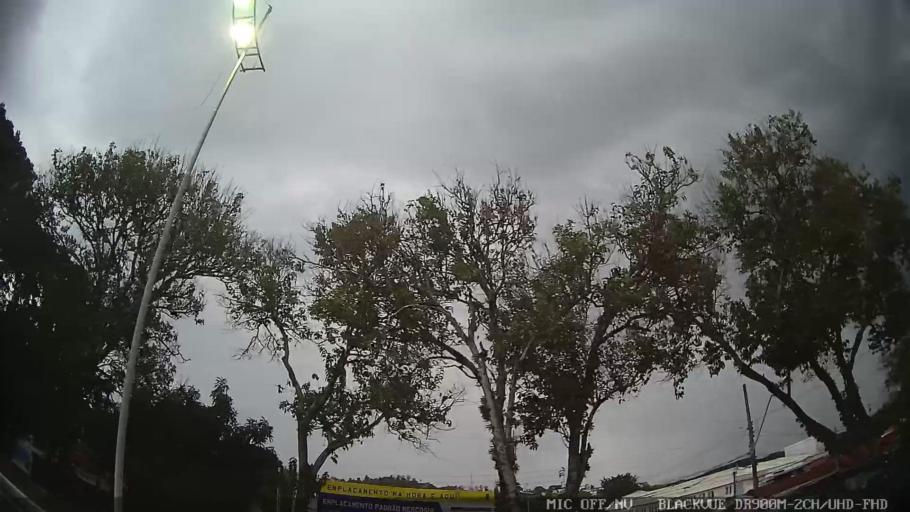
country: BR
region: Sao Paulo
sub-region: Amparo
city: Amparo
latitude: -22.7108
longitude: -46.7767
